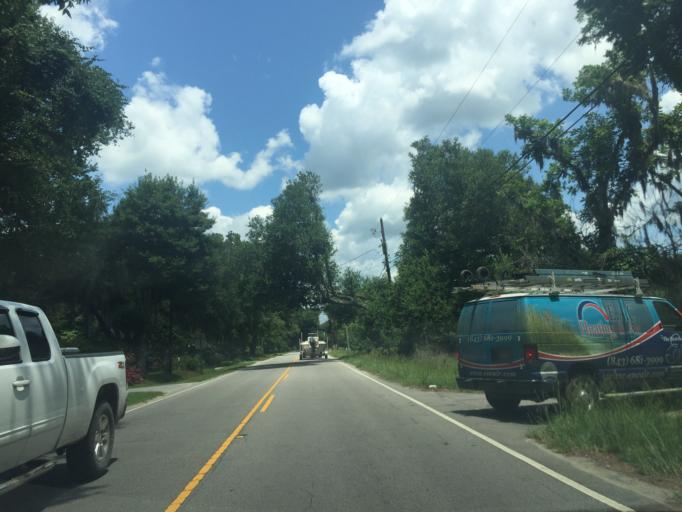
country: US
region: South Carolina
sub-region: Jasper County
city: Ridgeland
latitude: 32.4756
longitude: -80.9624
